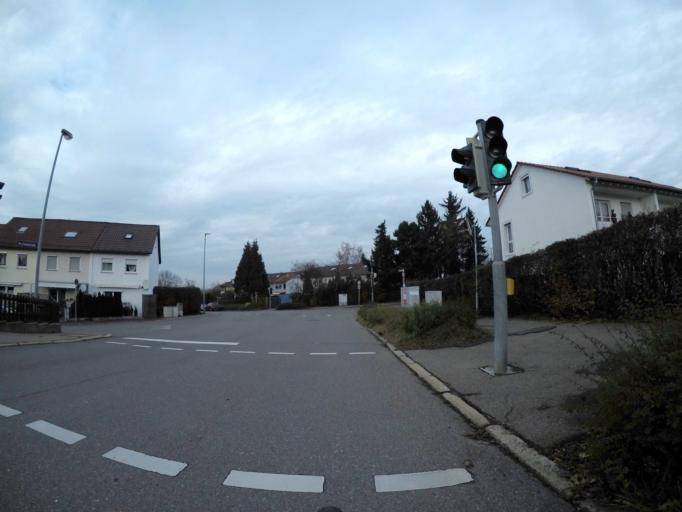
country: DE
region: Baden-Wuerttemberg
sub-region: Tuebingen Region
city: Reutlingen
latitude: 48.5046
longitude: 9.2292
